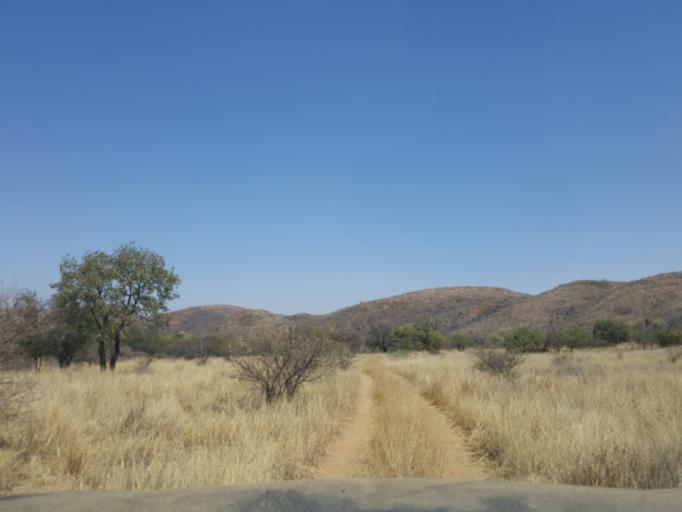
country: BW
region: South East
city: Lobatse
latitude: -25.1383
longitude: 25.6717
